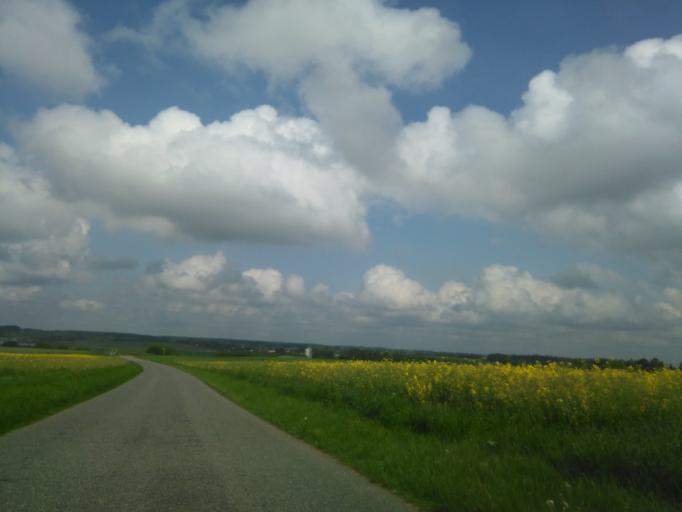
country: DK
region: Central Jutland
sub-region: Arhus Kommune
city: Sabro
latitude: 56.2047
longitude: 9.9925
